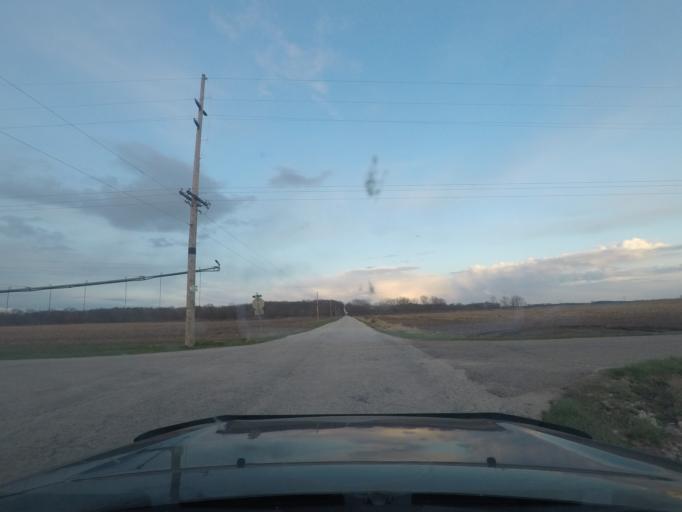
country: US
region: Indiana
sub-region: LaPorte County
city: Kingsford Heights
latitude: 41.4619
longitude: -86.7188
